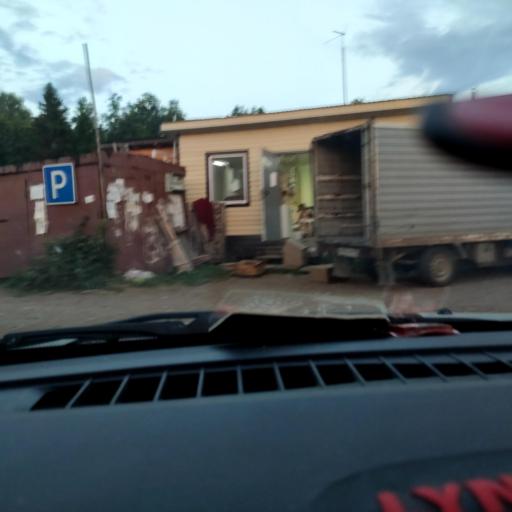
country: RU
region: Perm
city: Kukushtan
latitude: 57.6177
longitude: 56.4719
